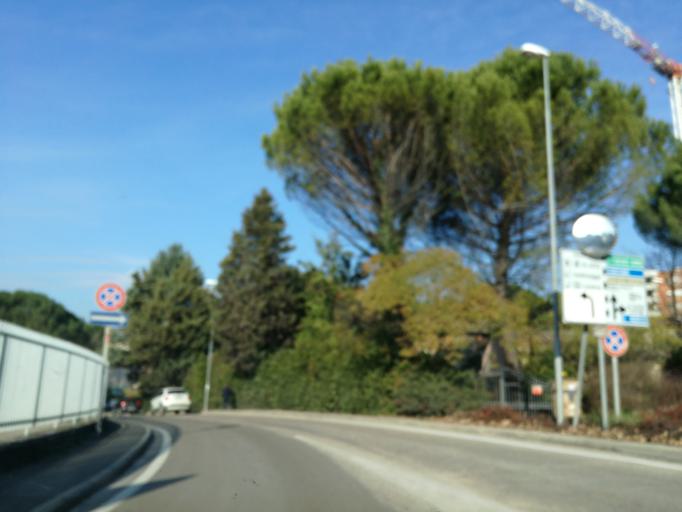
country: IT
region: Umbria
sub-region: Provincia di Perugia
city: Perugia
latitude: 43.1084
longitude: 12.3666
